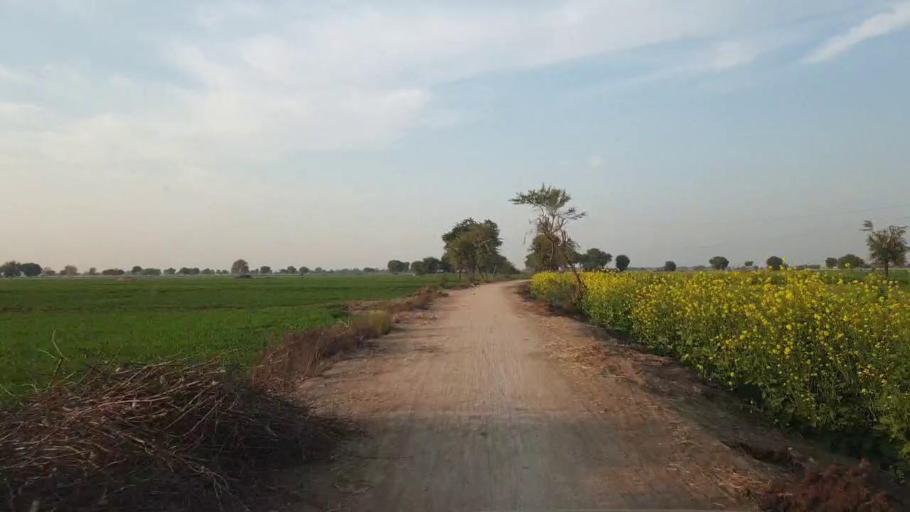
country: PK
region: Sindh
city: Shahpur Chakar
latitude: 26.1731
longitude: 68.6225
